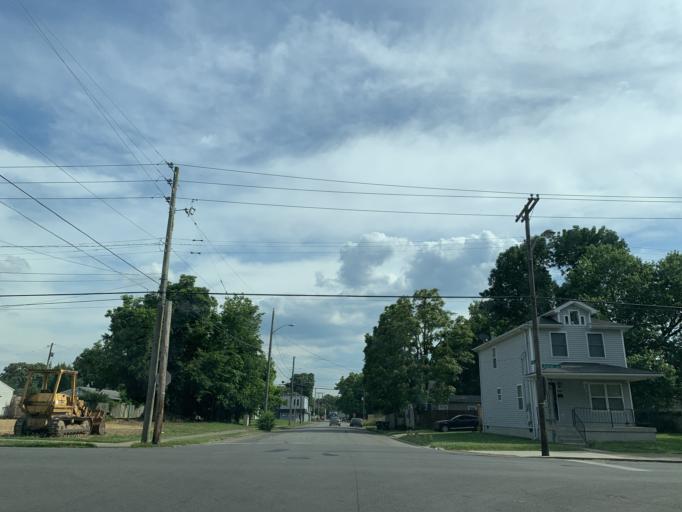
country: US
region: Kentucky
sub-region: Jefferson County
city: Louisville
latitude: 38.2631
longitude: -85.7892
